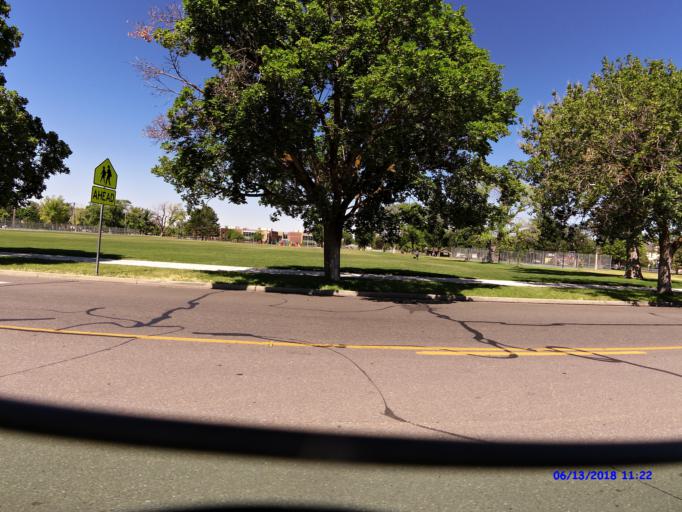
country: US
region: Utah
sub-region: Weber County
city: Ogden
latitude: 41.2280
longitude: -111.9592
